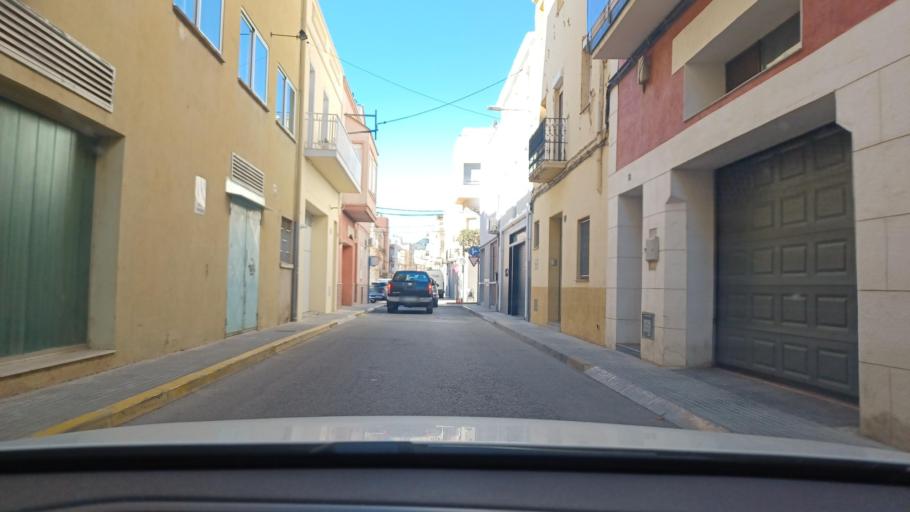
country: ES
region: Catalonia
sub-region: Provincia de Tarragona
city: Amposta
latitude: 40.7139
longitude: 0.5789
